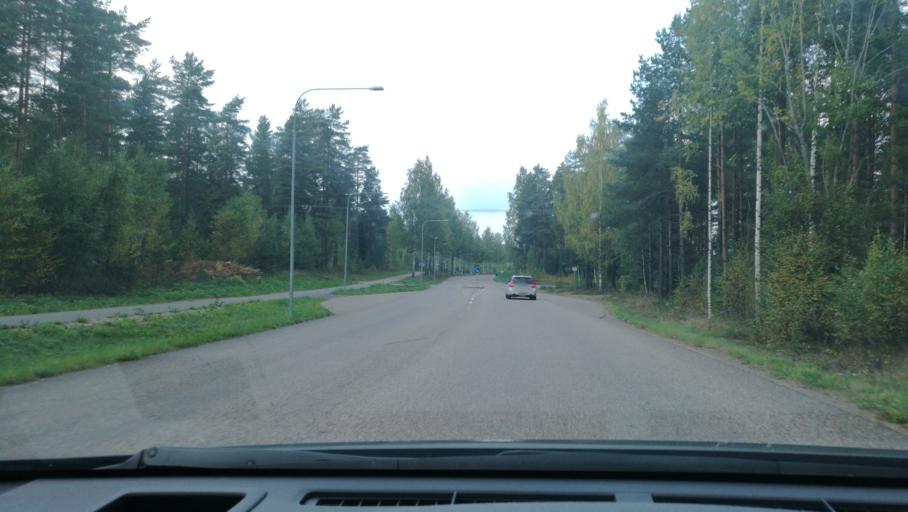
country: SE
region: Dalarna
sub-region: Avesta Kommun
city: Avesta
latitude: 60.1564
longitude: 16.1988
